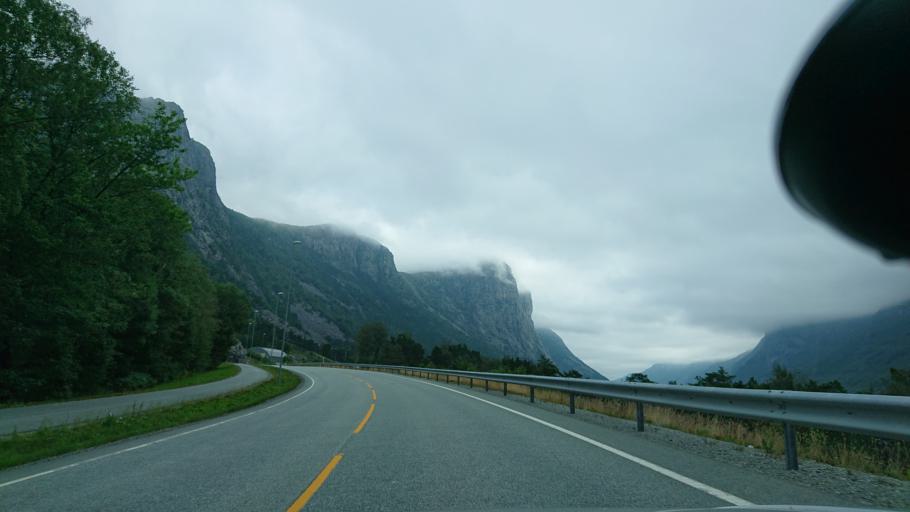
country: NO
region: Rogaland
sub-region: Strand
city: Jorpeland
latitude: 59.0752
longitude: 6.0643
